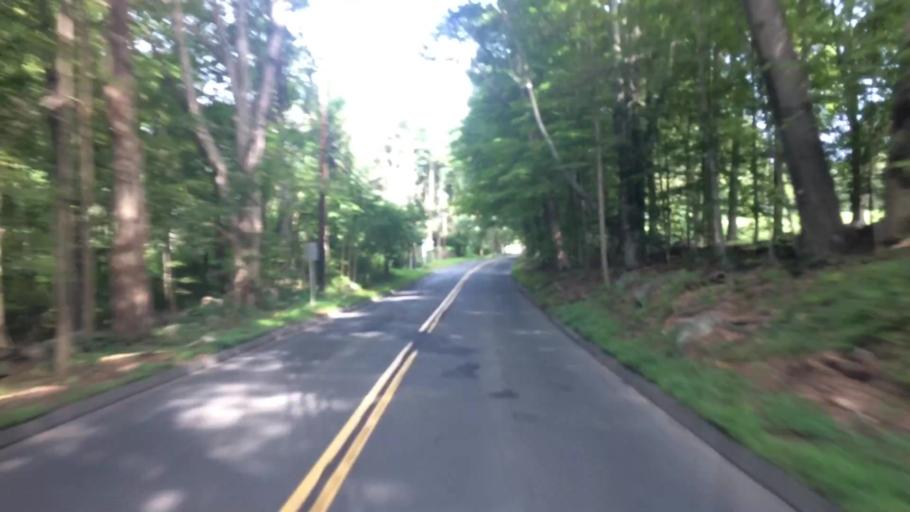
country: US
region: Connecticut
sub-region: Fairfield County
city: Danbury
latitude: 41.4040
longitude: -73.4766
